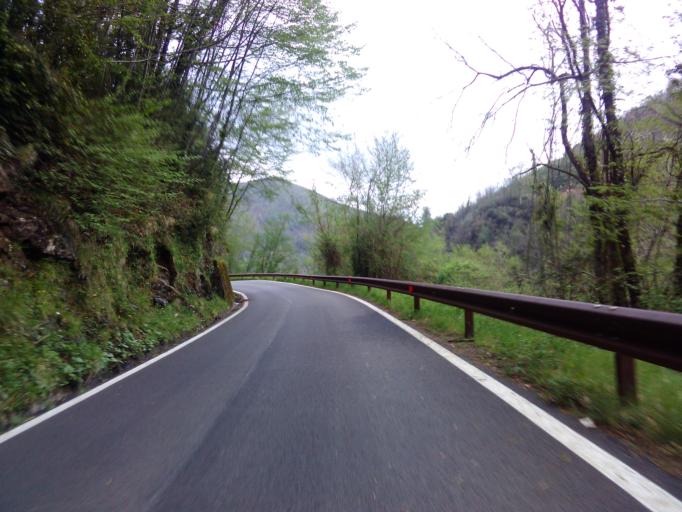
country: IT
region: Tuscany
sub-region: Provincia di Lucca
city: Pontestazzemese
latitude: 43.9753
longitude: 10.2756
